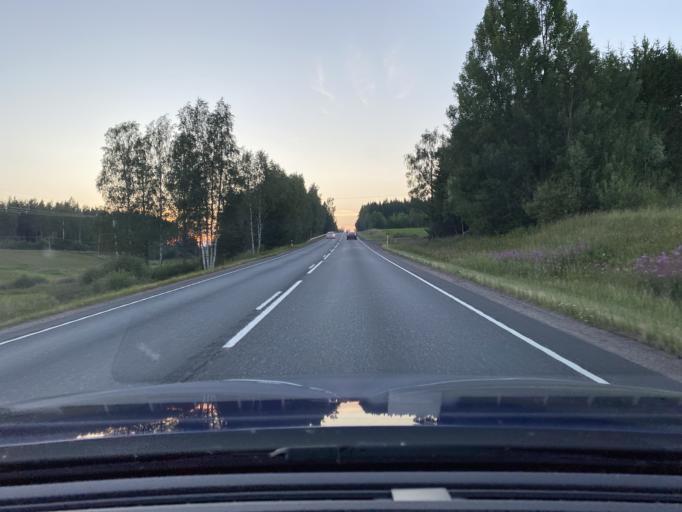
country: FI
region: Pirkanmaa
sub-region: Luoteis-Pirkanmaa
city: Ikaalinen
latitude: 61.8149
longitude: 22.9559
